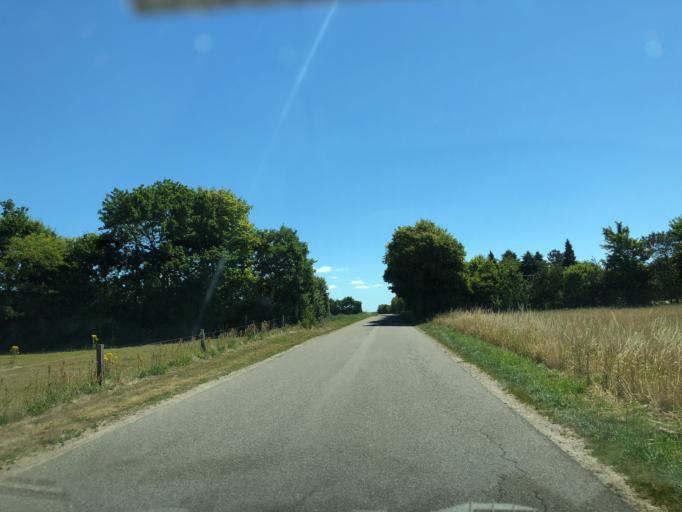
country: DK
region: Central Jutland
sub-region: Viborg Kommune
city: Viborg
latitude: 56.5580
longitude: 9.4187
